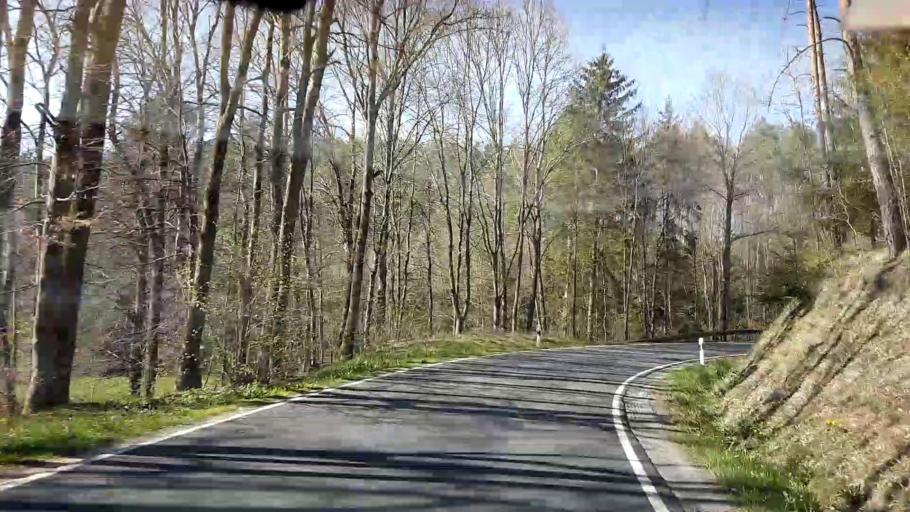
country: DE
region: Bavaria
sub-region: Upper Franconia
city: Pottenstein
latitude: 49.7956
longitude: 11.3769
